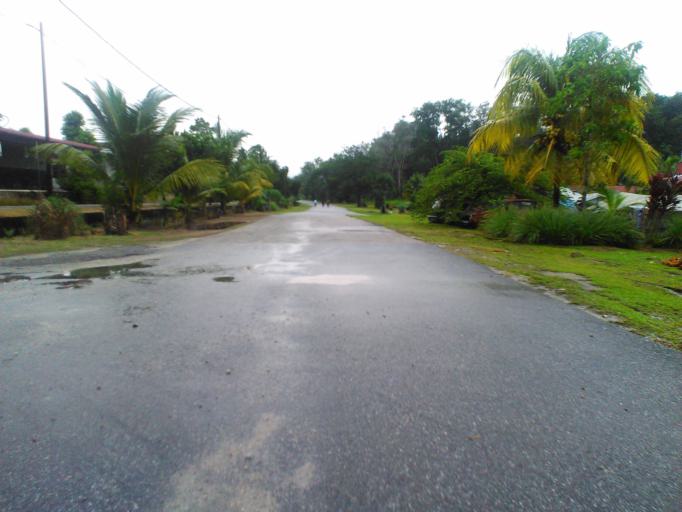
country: MY
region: Kedah
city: Kulim
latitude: 5.3618
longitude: 100.5781
